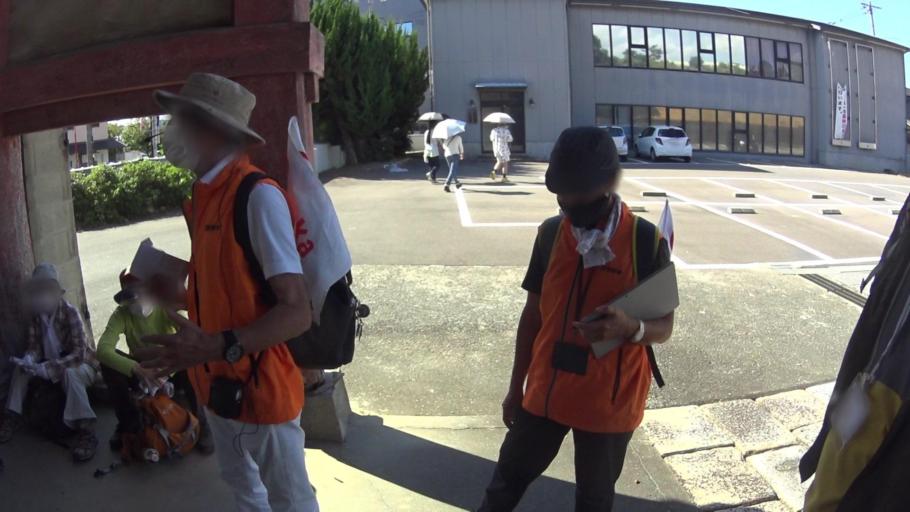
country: JP
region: Ehime
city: Kihoku-cho
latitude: 33.3777
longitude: 132.8145
